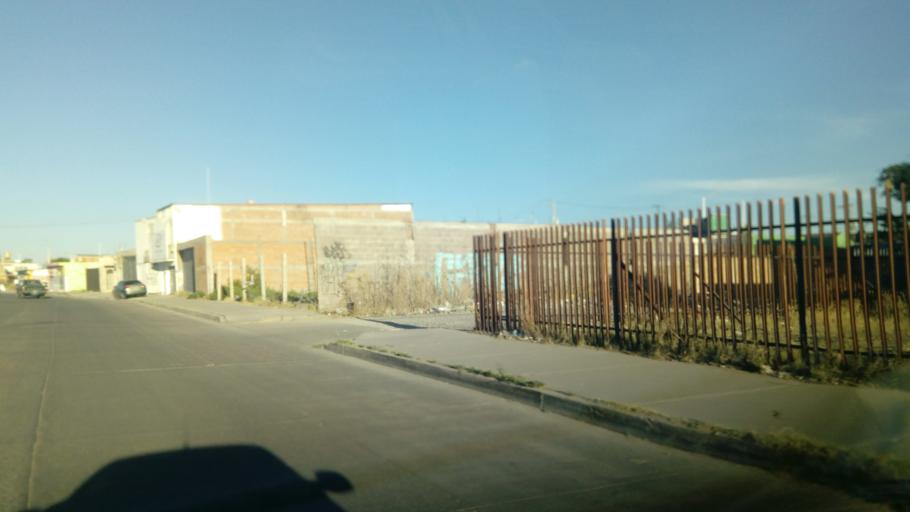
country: MX
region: Durango
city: Victoria de Durango
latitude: 24.0558
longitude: -104.5930
